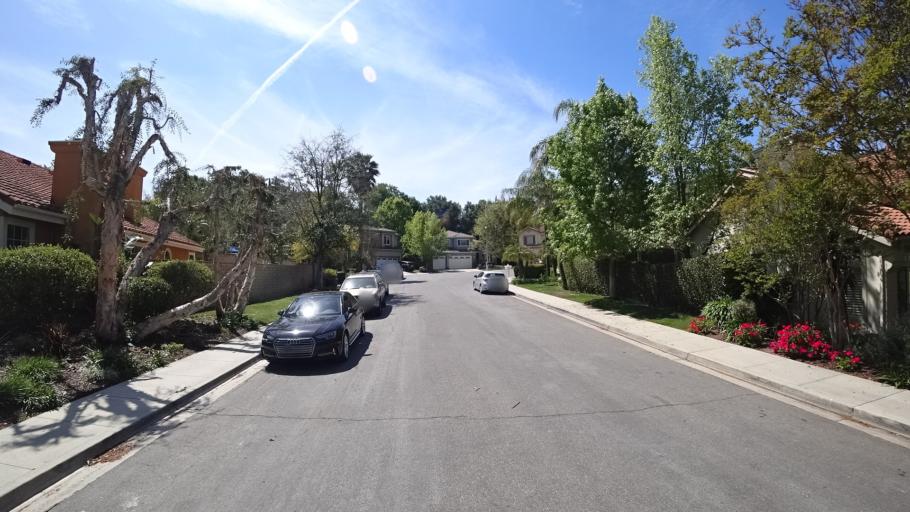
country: US
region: California
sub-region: Ventura County
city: Thousand Oaks
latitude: 34.2018
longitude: -118.8429
